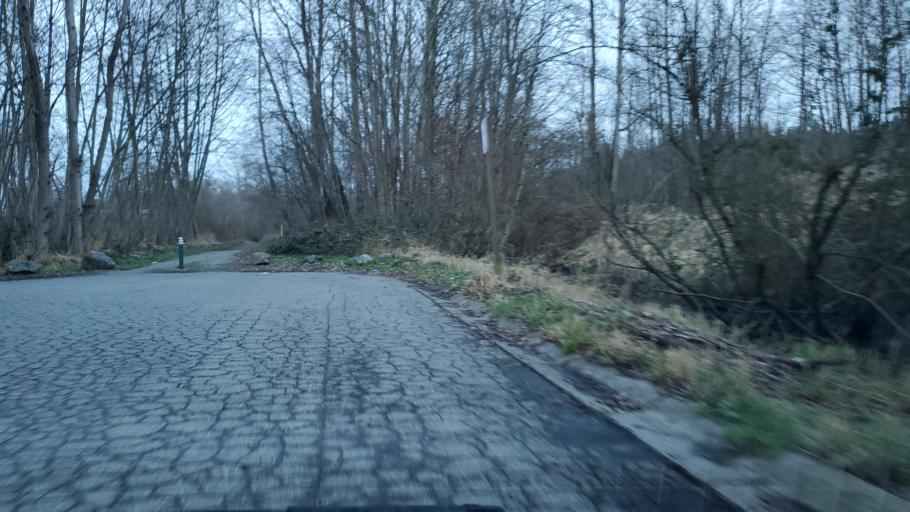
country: US
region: Washington
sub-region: Skagit County
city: Mount Vernon
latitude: 48.4330
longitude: -122.3284
